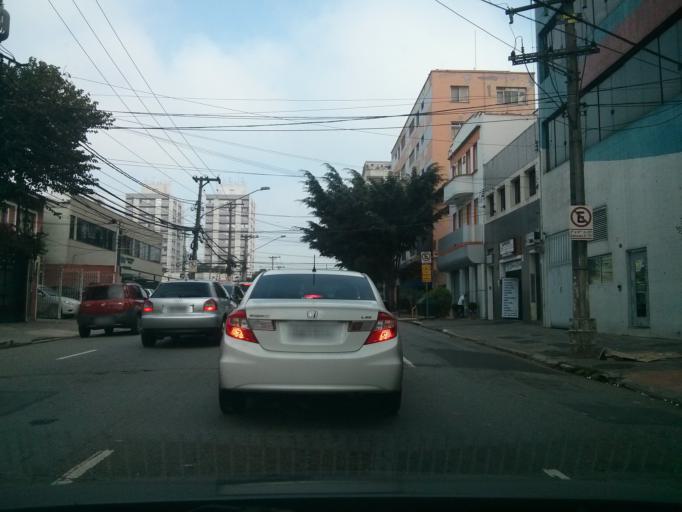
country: BR
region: Sao Paulo
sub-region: Sao Paulo
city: Sao Paulo
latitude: -23.6015
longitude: -46.6358
